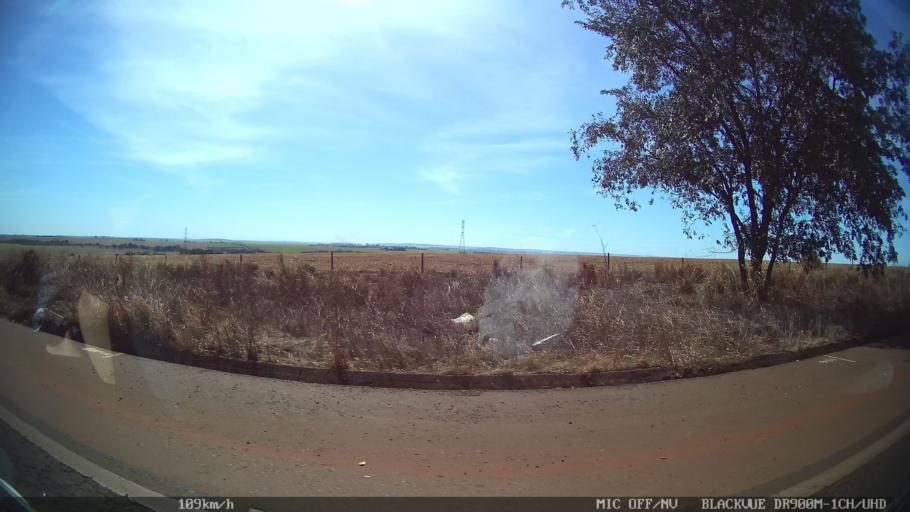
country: BR
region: Sao Paulo
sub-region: Sao Joaquim Da Barra
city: Sao Joaquim da Barra
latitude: -20.5184
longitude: -47.8737
